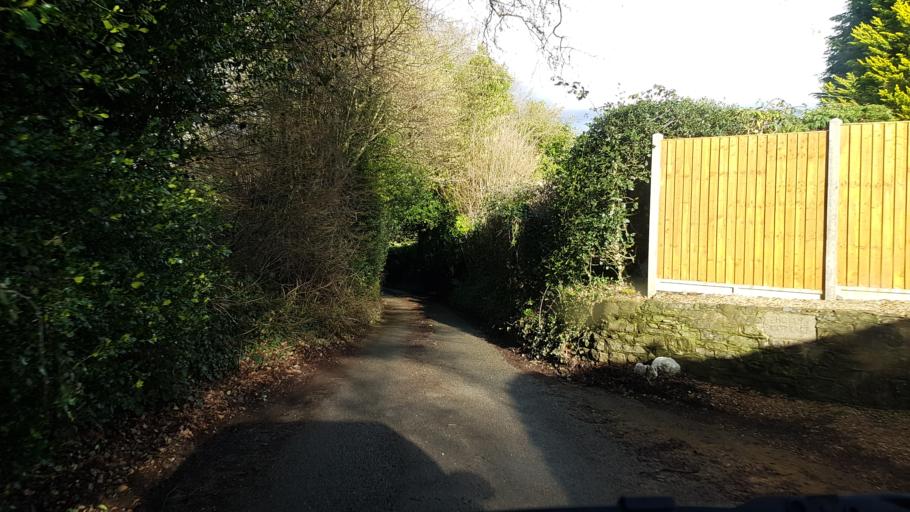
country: GB
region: England
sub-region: Surrey
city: Churt
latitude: 51.1311
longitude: -0.7831
